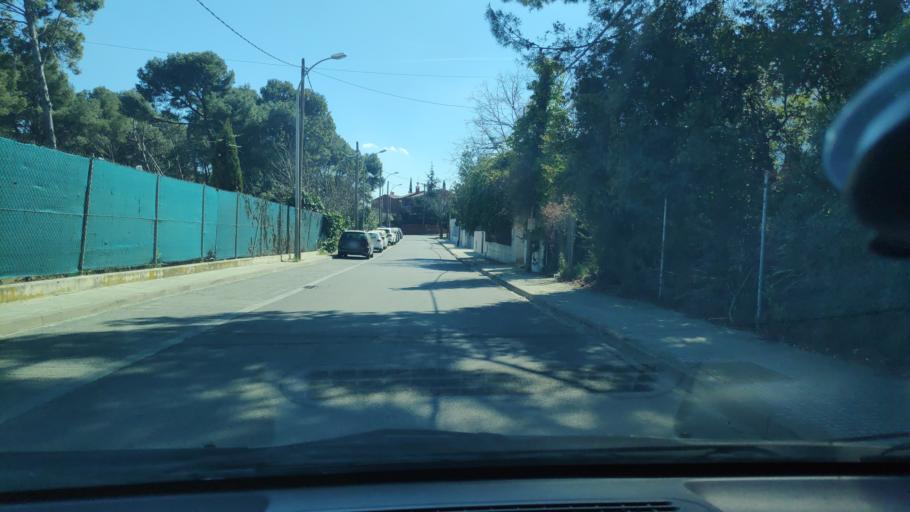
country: ES
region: Catalonia
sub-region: Provincia de Barcelona
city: Rubi
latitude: 41.5287
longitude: 2.0314
